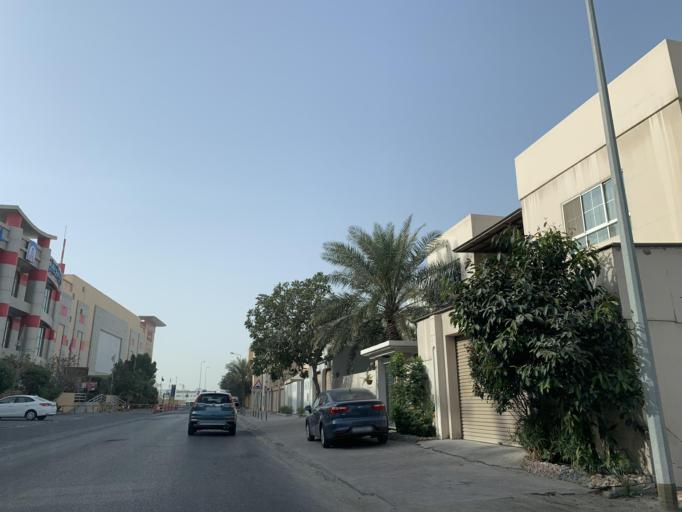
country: BH
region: Northern
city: Madinat `Isa
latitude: 26.1632
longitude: 50.5223
